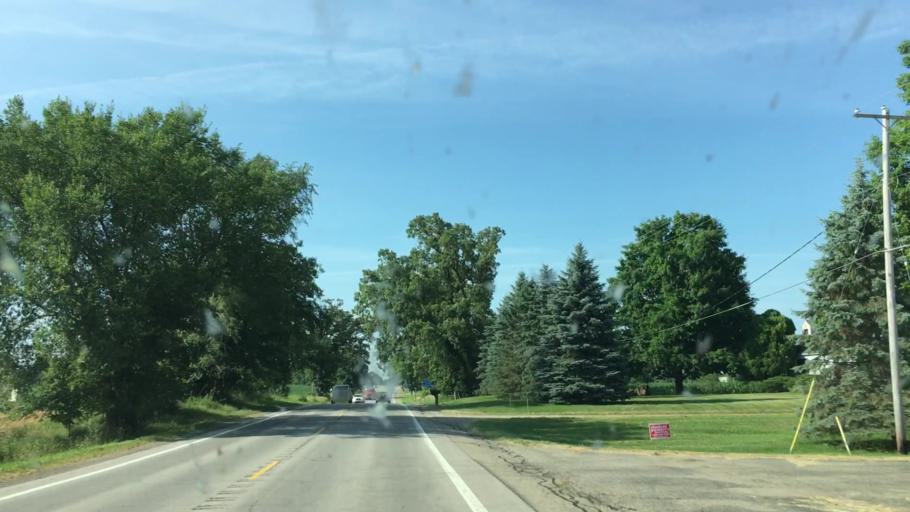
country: US
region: Michigan
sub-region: Kalamazoo County
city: South Gull Lake
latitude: 42.3952
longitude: -85.4552
